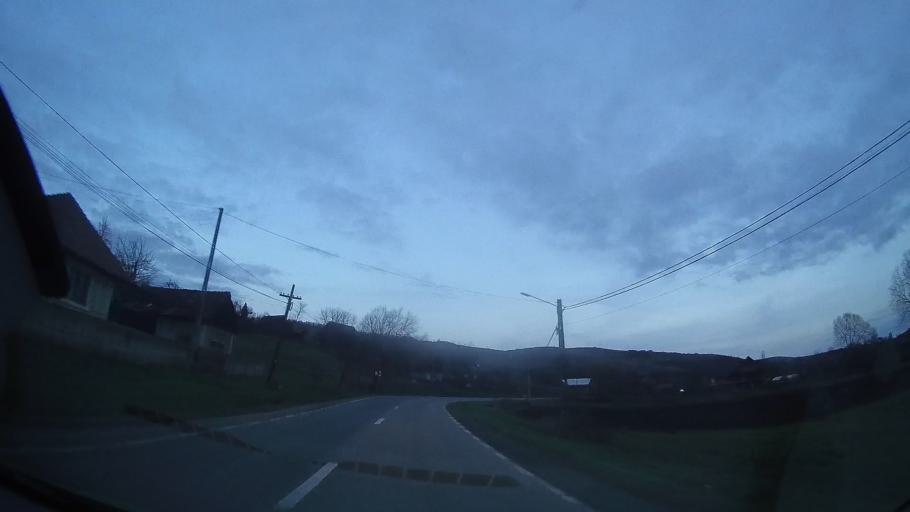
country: RO
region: Cluj
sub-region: Comuna Caianu
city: Vaida-Camaras
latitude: 46.8062
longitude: 23.9643
